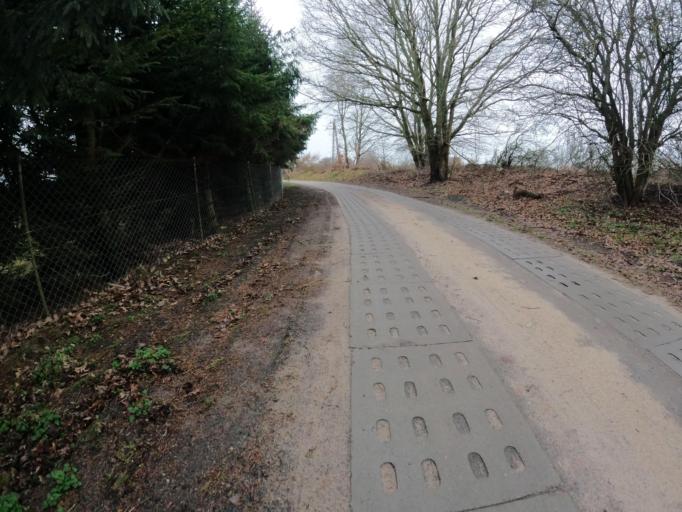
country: PL
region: West Pomeranian Voivodeship
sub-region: Powiat slawienski
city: Darlowo
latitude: 54.4130
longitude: 16.4356
